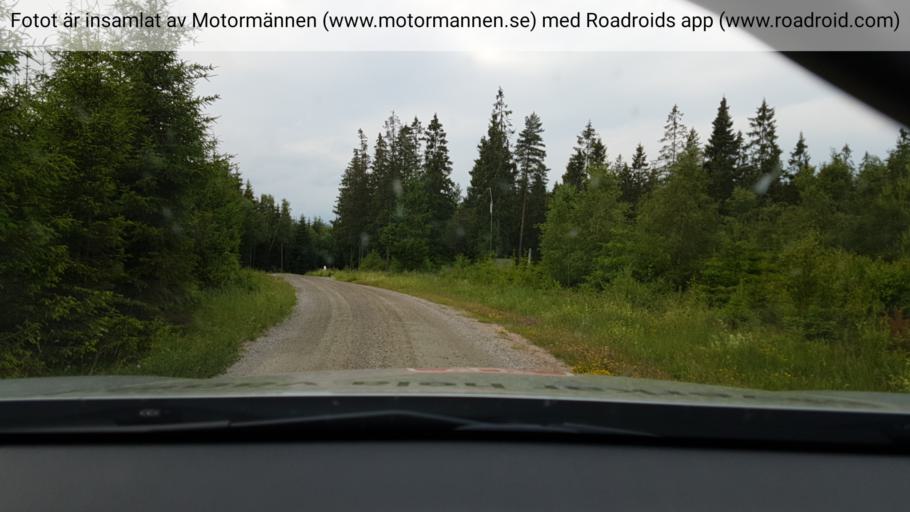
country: SE
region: Joenkoeping
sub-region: Mullsjo Kommun
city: Mullsjoe
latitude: 57.9194
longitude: 13.7162
